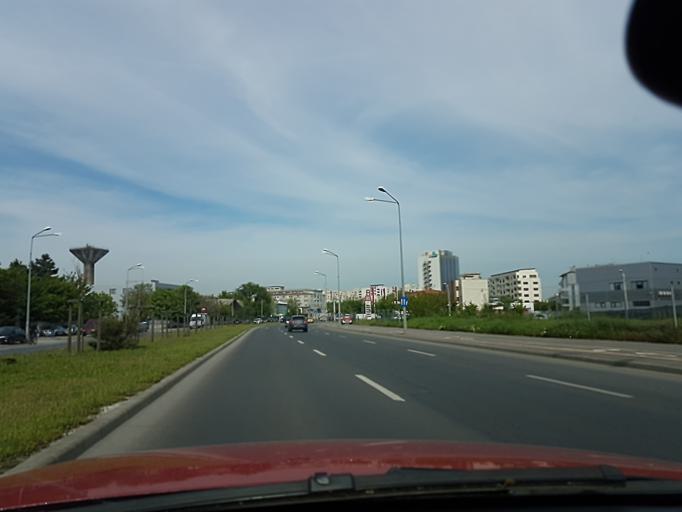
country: RO
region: Bucuresti
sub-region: Municipiul Bucuresti
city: Bucuresti
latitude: 44.4195
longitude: 26.0776
